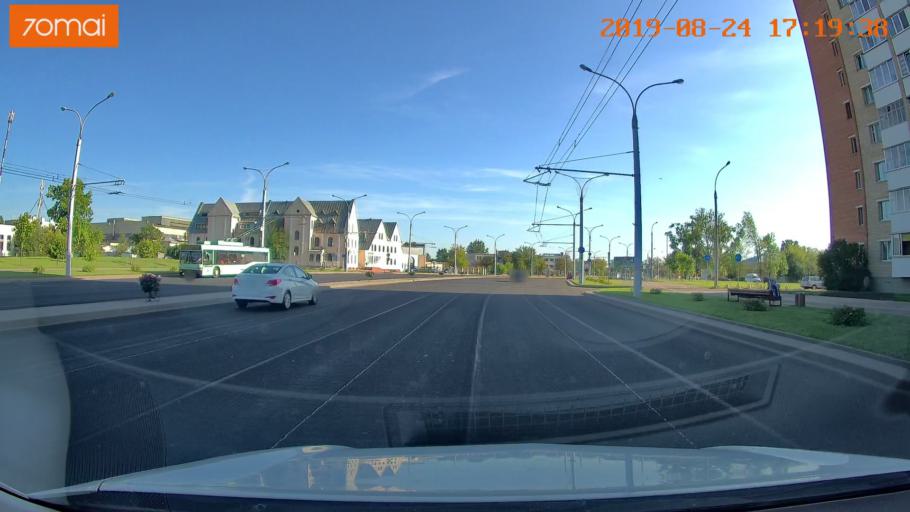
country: BY
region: Minsk
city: Vyaliki Trastsyanets
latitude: 53.8601
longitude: 27.6410
